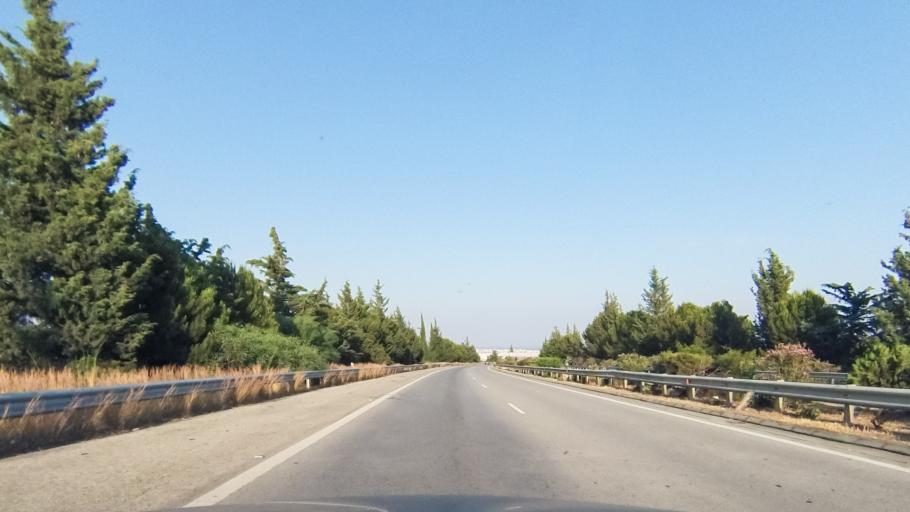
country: CY
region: Limassol
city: Ypsonas
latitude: 34.6971
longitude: 32.9614
